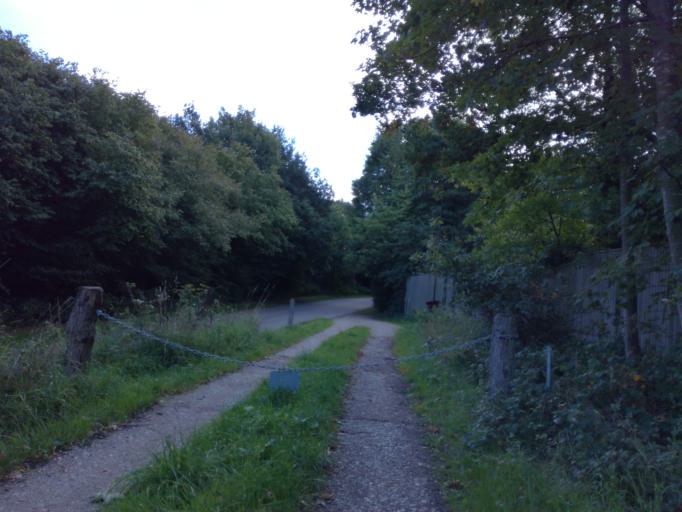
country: DK
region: South Denmark
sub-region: Fredericia Kommune
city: Snoghoj
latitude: 55.5131
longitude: 9.6976
